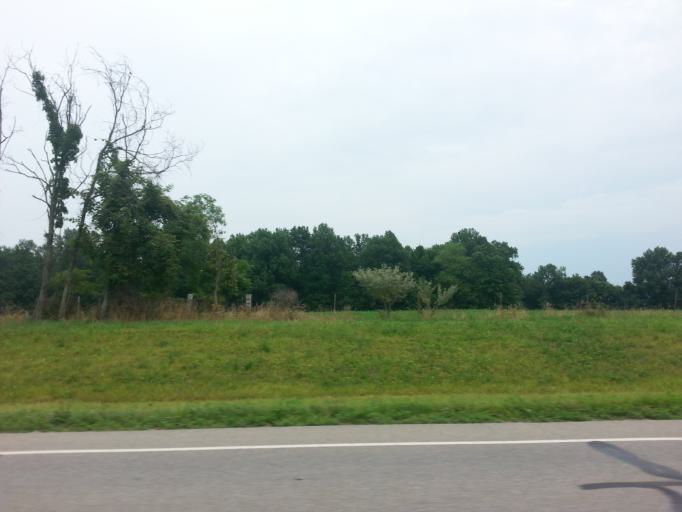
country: US
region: Ohio
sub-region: Brown County
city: Georgetown
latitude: 38.8826
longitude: -83.8907
